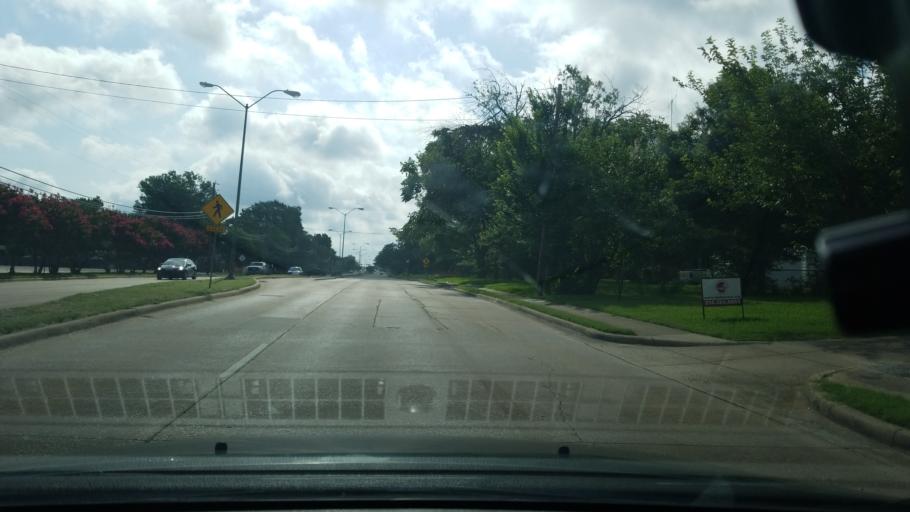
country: US
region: Texas
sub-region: Dallas County
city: Mesquite
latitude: 32.8214
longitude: -96.6646
